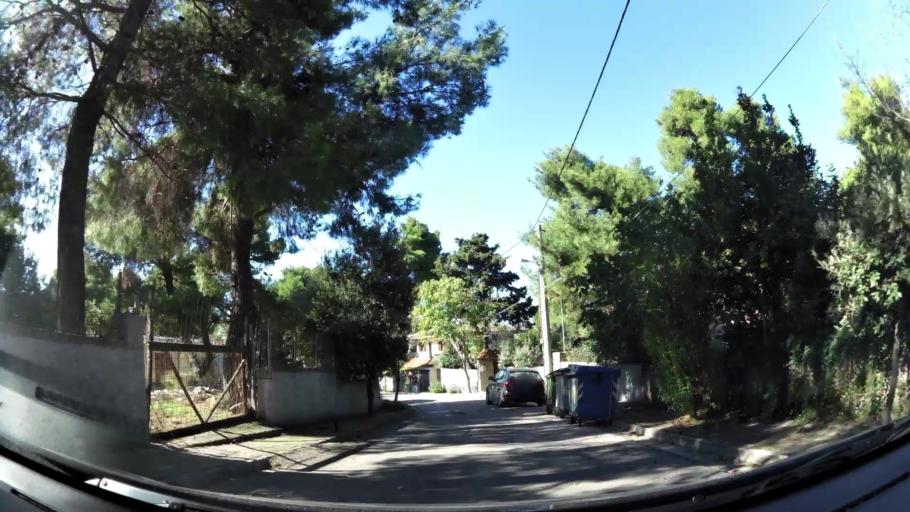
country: GR
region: Attica
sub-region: Nomarchia Anatolikis Attikis
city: Rodopoli
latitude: 38.1151
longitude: 23.8790
